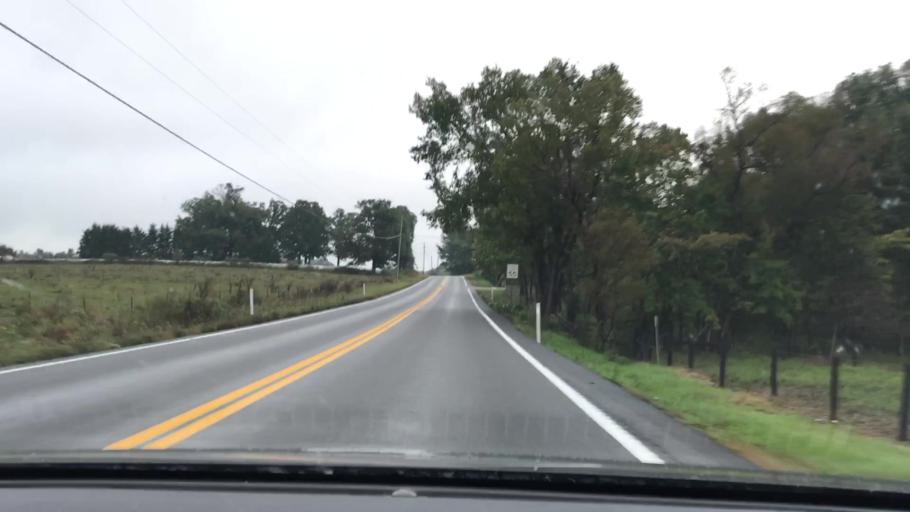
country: US
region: Tennessee
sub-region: Fentress County
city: Grimsley
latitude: 36.1591
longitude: -85.0710
